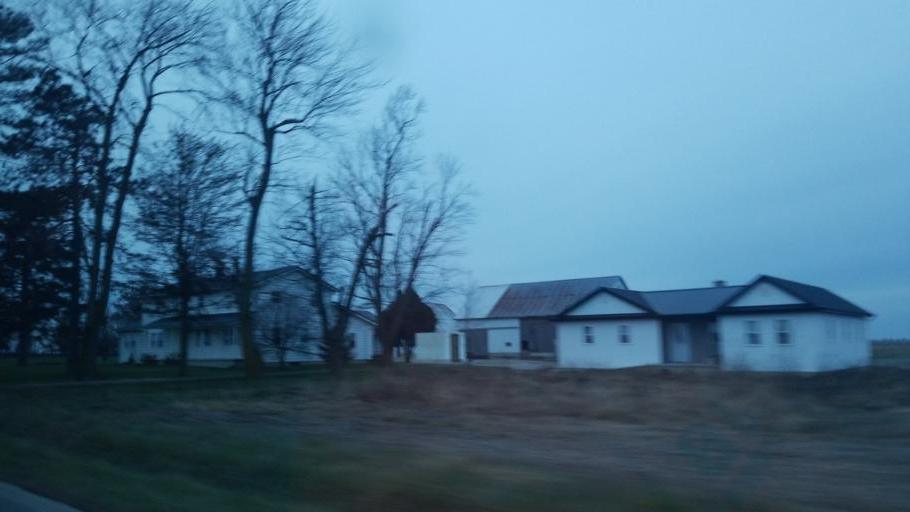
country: US
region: Indiana
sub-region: Adams County
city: Berne
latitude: 40.7313
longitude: -84.9100
